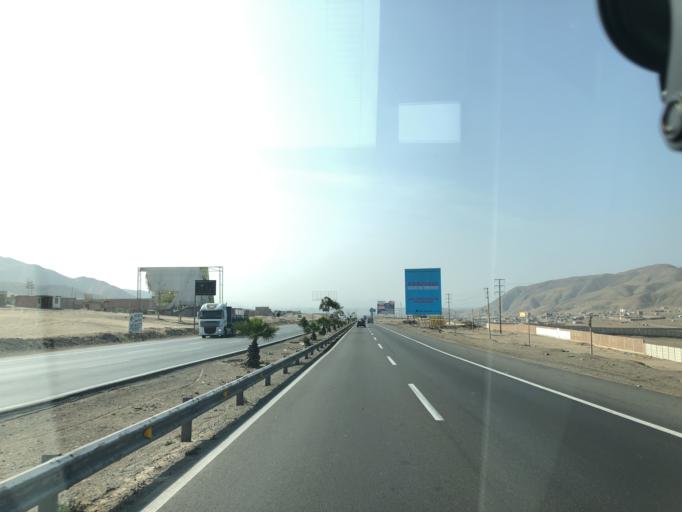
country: PE
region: Lima
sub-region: Lima
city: Pucusana
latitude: -12.4460
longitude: -76.7566
